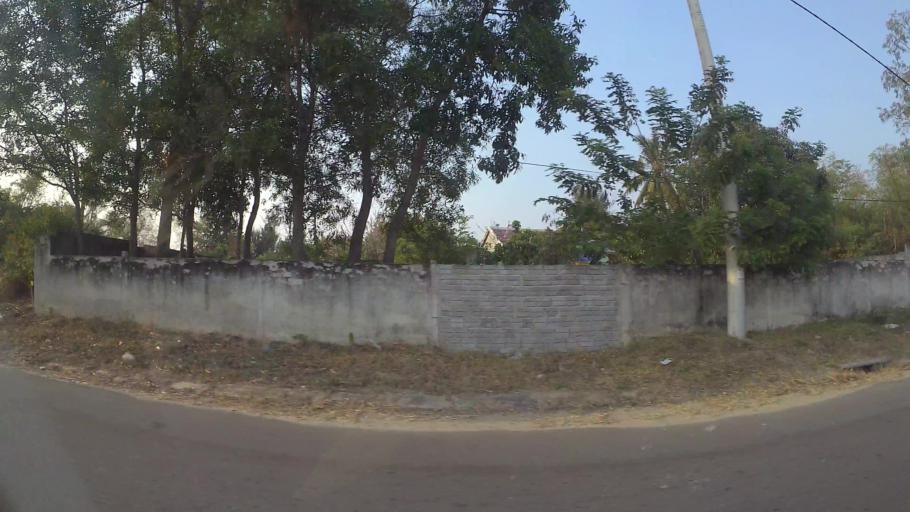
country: VN
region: Da Nang
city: Ngu Hanh Son
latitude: 15.9777
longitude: 108.2374
